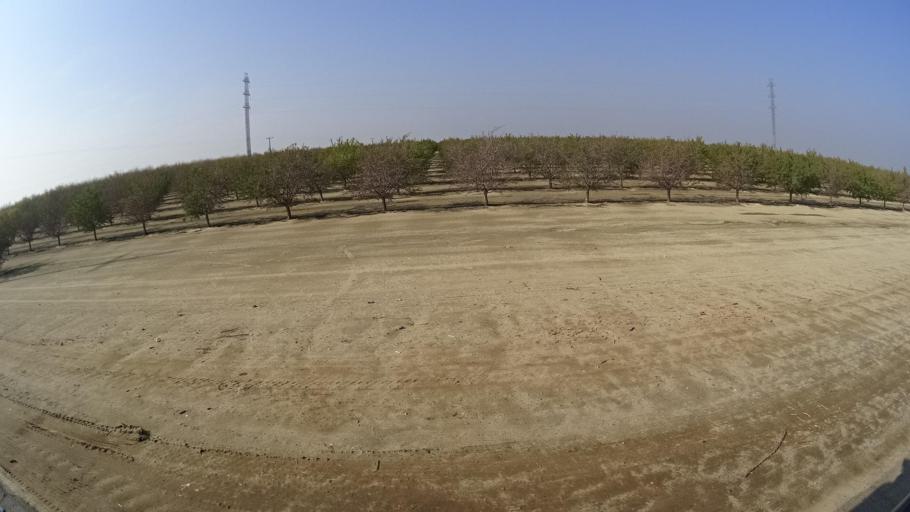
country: US
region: California
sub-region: Kern County
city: Buttonwillow
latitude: 35.4284
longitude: -119.4471
